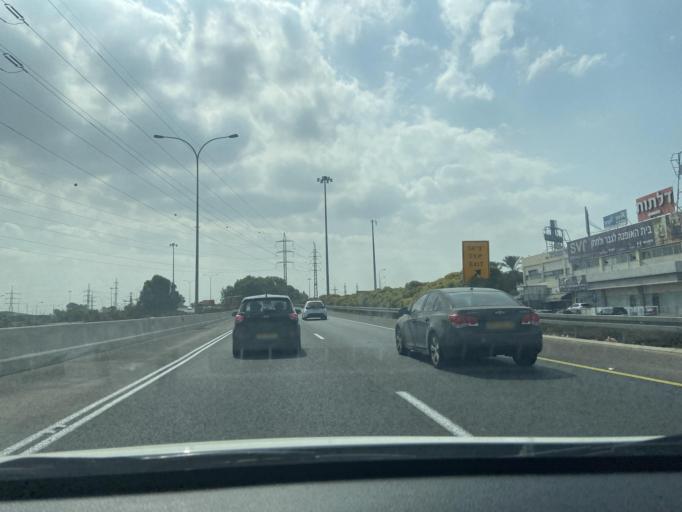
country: IL
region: Haifa
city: Qiryat Yam
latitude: 32.8780
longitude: 35.0968
